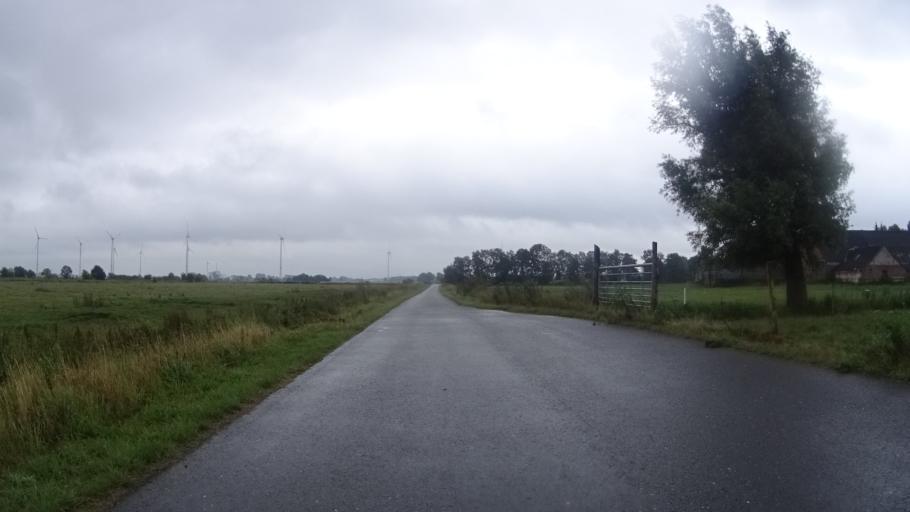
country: DE
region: Lower Saxony
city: Weener
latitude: 53.1806
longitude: 7.3171
